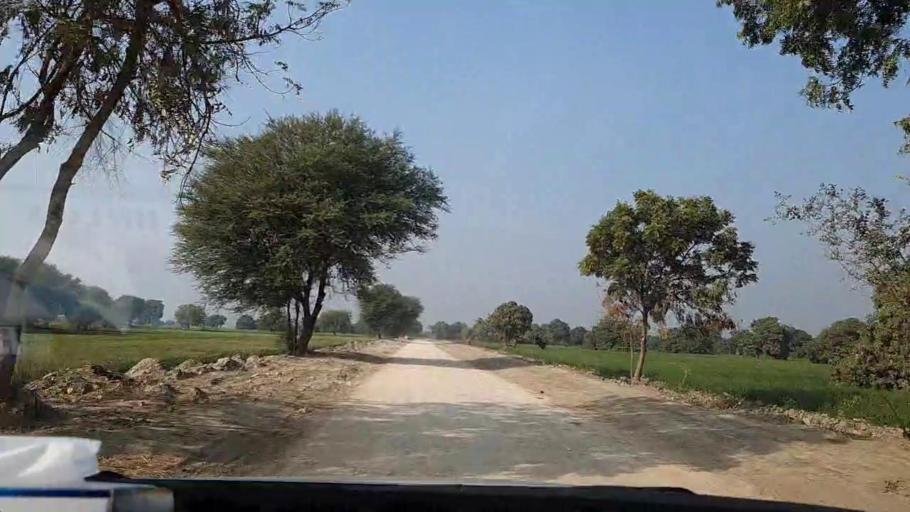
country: PK
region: Sindh
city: Tando Ghulam Ali
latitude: 25.1448
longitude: 68.8767
